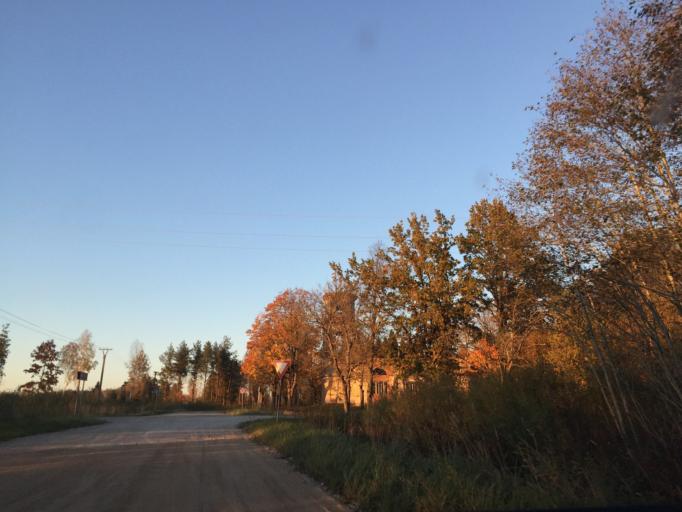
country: LT
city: Vieksniai
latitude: 56.3955
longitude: 22.5565
